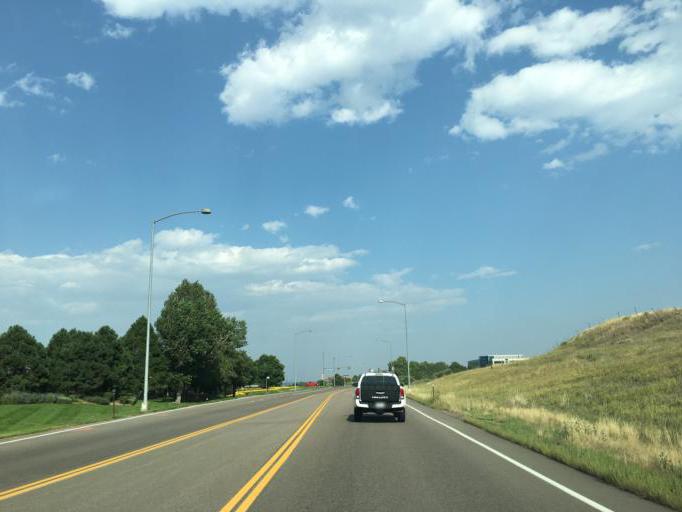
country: US
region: Colorado
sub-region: Broomfield County
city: Broomfield
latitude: 39.9166
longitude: -105.1140
